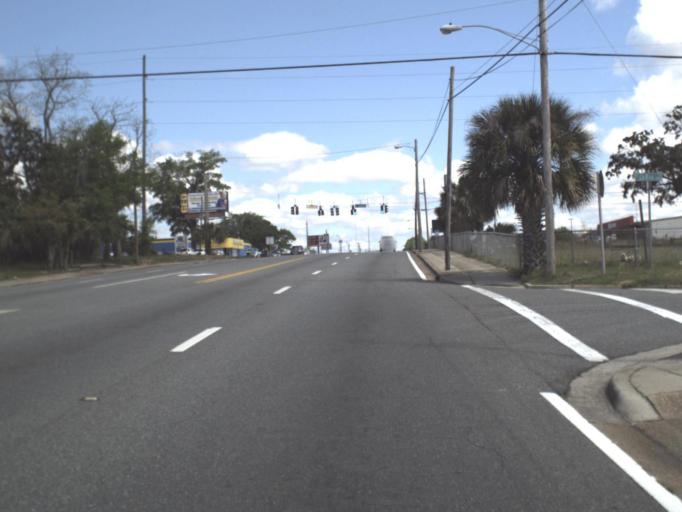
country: US
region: Florida
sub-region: Escambia County
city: Pensacola
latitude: 30.4175
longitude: -87.2414
